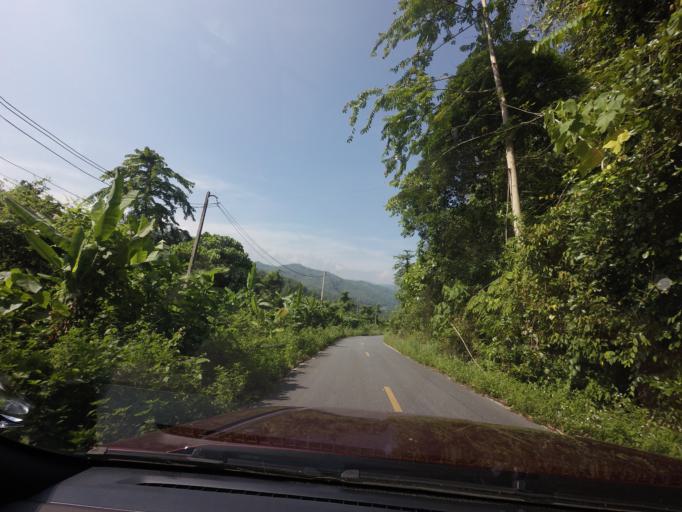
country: TH
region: Yala
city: Than To
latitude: 5.9889
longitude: 101.2014
